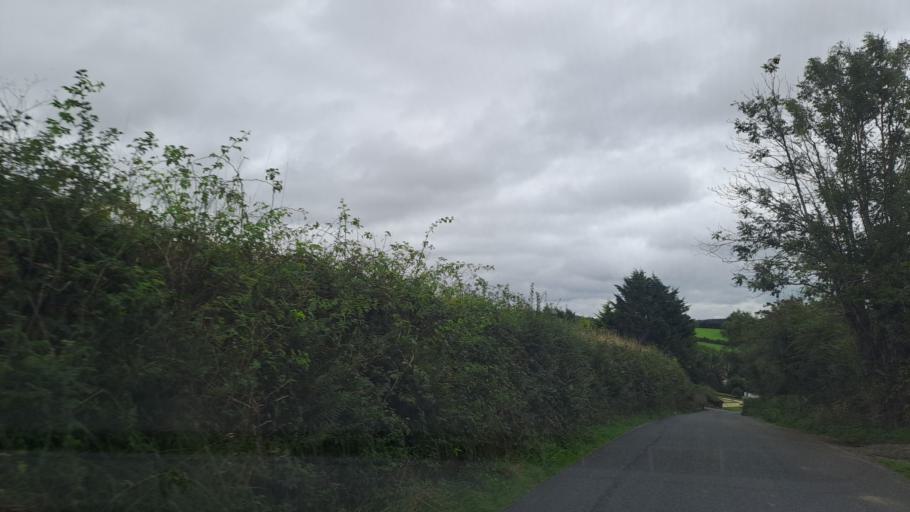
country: IE
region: Ulster
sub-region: An Cabhan
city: Bailieborough
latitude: 54.0010
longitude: -6.8942
